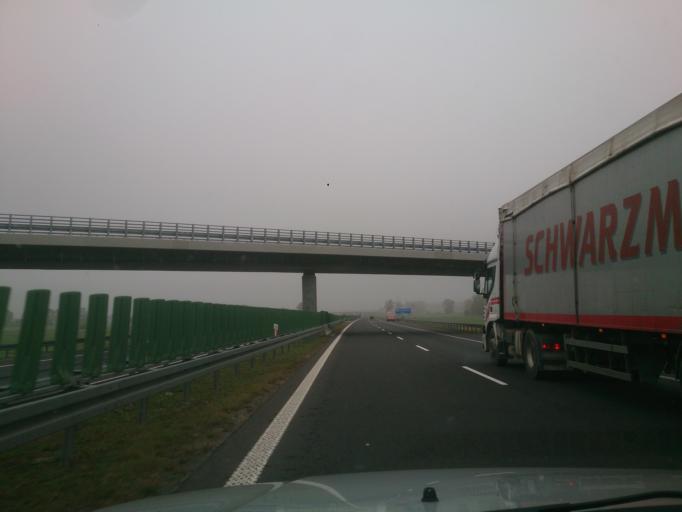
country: PL
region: Pomeranian Voivodeship
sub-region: Powiat starogardzki
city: Smetowo Graniczne
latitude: 53.7033
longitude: 18.6280
